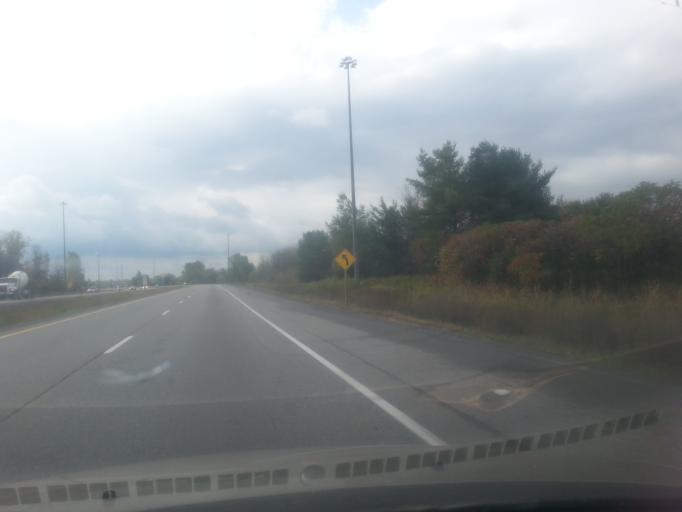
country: CA
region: Ontario
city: Bells Corners
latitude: 45.3225
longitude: -75.8059
